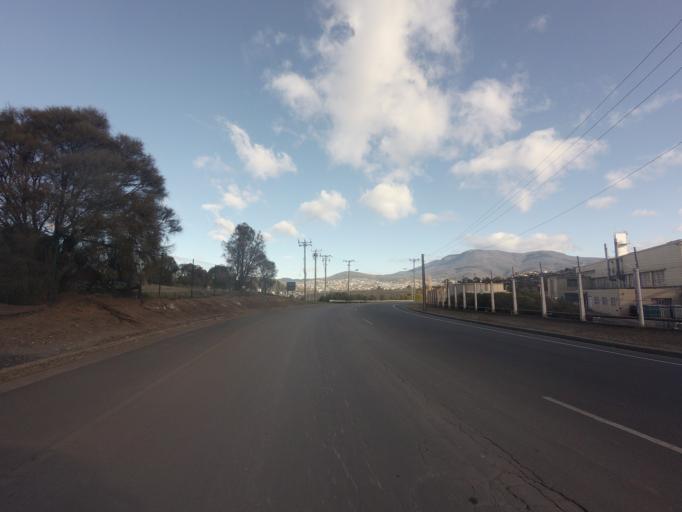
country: AU
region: Tasmania
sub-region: Glenorchy
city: Lutana
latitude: -42.8361
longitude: 147.3219
